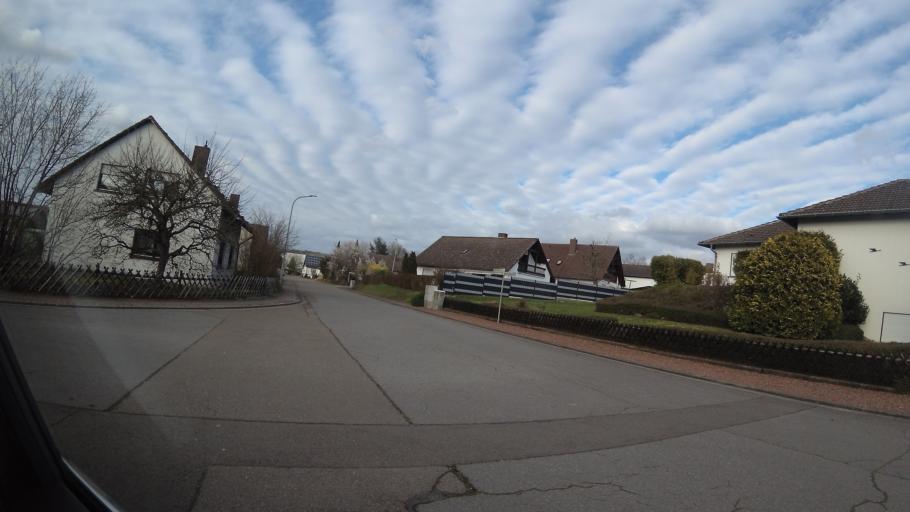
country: DE
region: Saarland
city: Blieskastel
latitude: 49.2280
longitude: 7.2727
